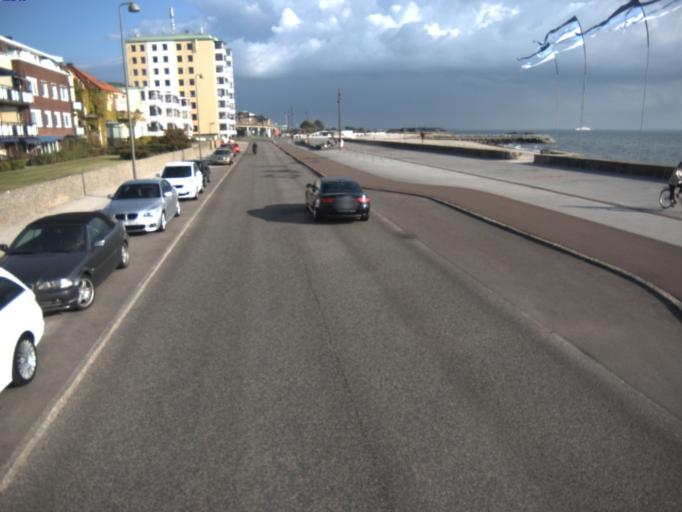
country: SE
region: Skane
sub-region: Helsingborg
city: Helsingborg
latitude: 56.0604
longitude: 12.6808
